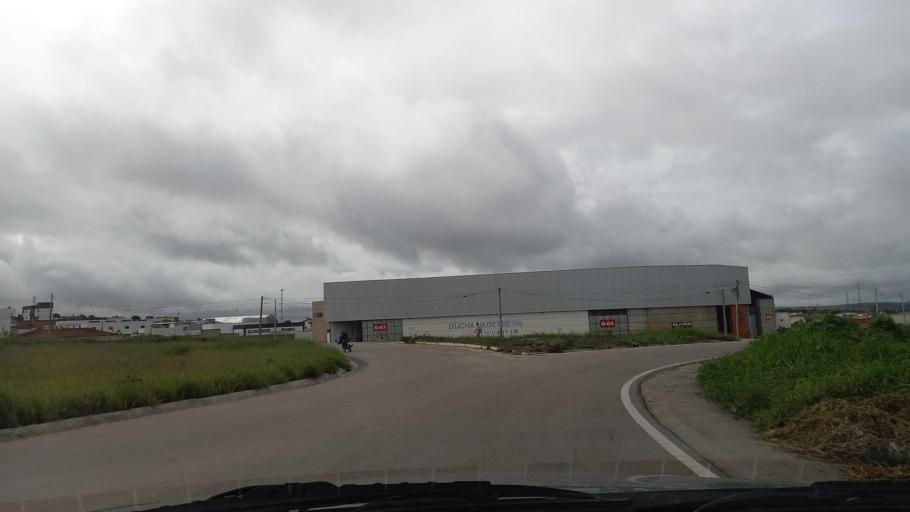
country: BR
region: Pernambuco
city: Garanhuns
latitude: -8.9079
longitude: -36.4879
